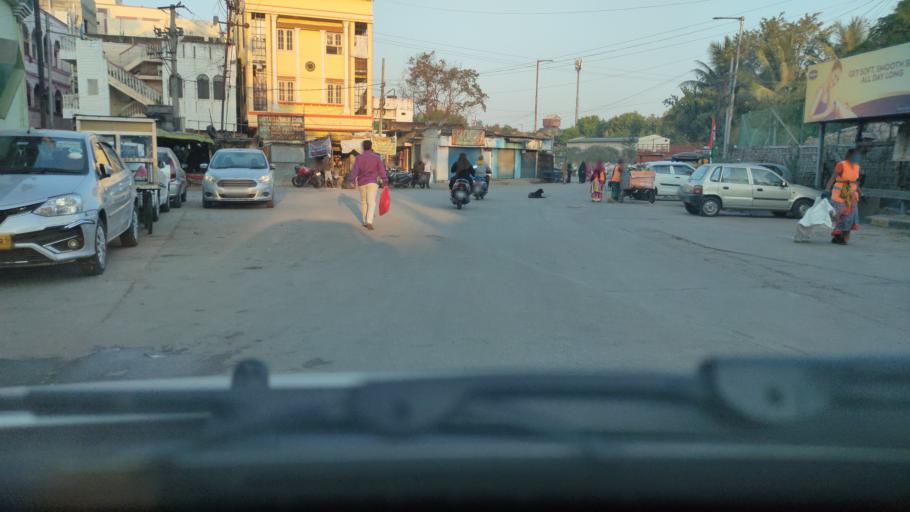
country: IN
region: Telangana
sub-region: Rangareddi
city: Gaddi Annaram
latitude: 17.3861
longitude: 78.5242
